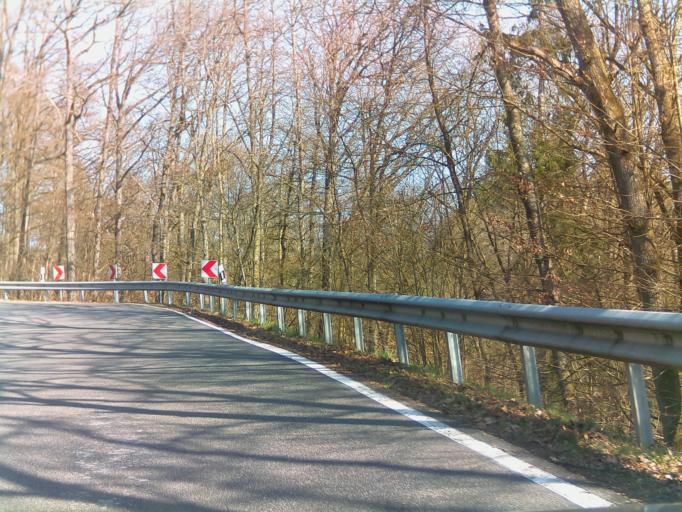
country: DE
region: Rheinland-Pfalz
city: Frauenberg
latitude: 49.6743
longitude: 7.2807
